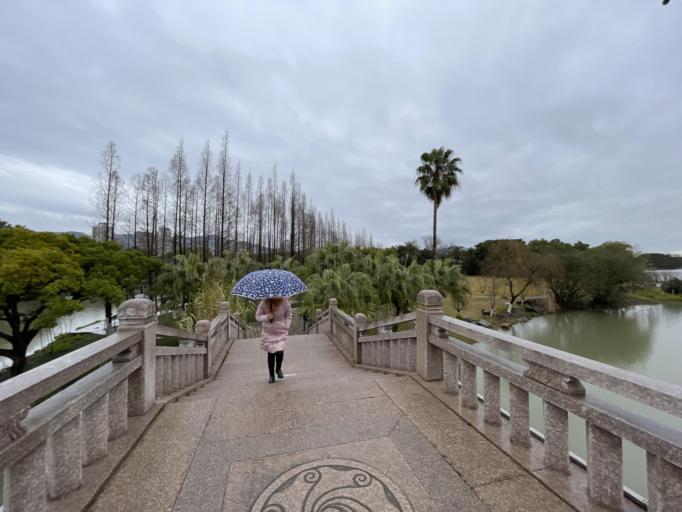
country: CN
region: Zhejiang Sheng
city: Oubei
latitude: 28.0317
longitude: 120.6399
